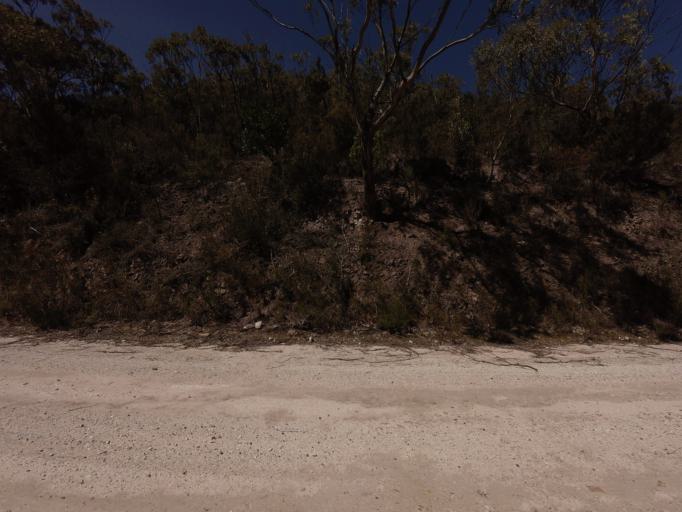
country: AU
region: Tasmania
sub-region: Huon Valley
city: Geeveston
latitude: -42.9255
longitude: 146.3479
